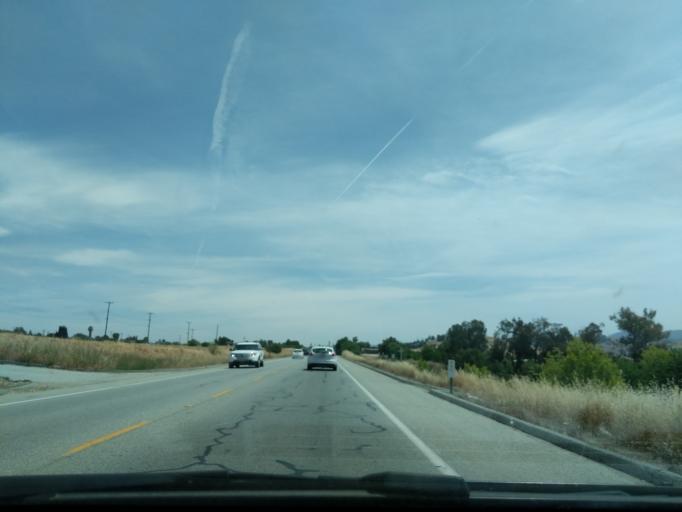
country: US
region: California
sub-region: San Benito County
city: Hollister
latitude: 36.8316
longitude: -121.3858
